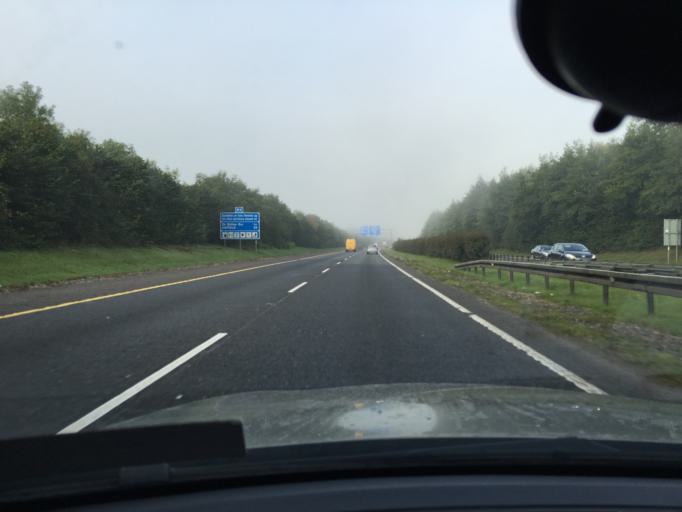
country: IE
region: Leinster
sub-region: Kildare
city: Leixlip
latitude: 53.3576
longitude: -6.5056
